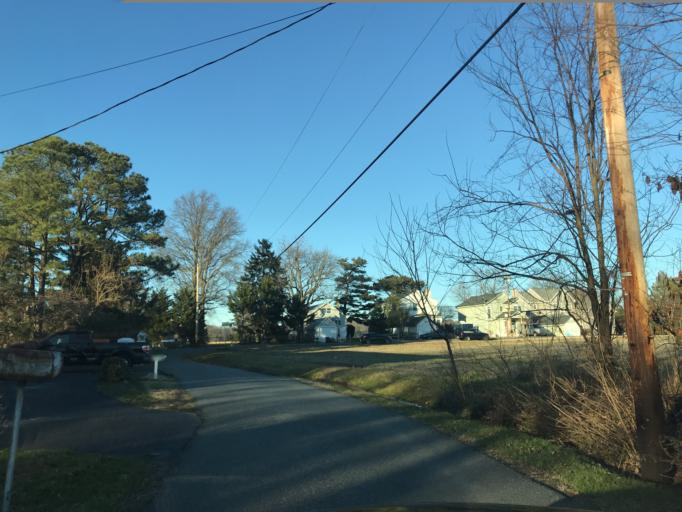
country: US
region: Maryland
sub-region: Baltimore County
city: Bowleys Quarters
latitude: 39.3307
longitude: -76.3680
